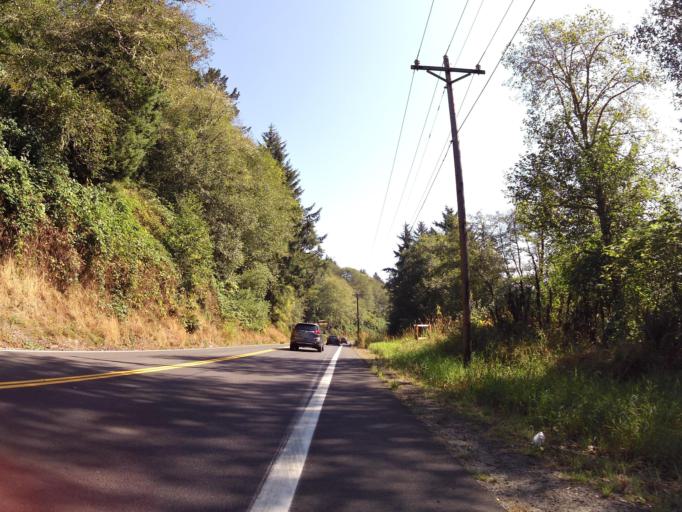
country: US
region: Oregon
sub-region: Tillamook County
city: Pacific City
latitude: 45.1899
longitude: -123.9505
